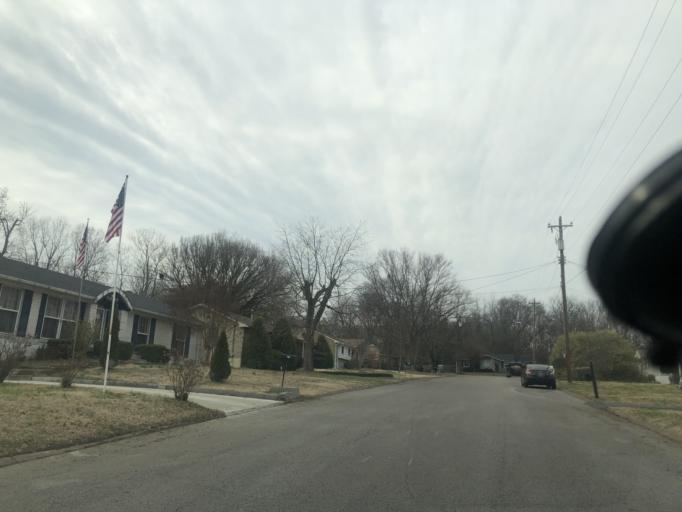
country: US
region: Tennessee
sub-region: Davidson County
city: Oak Hill
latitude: 36.0936
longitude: -86.7214
